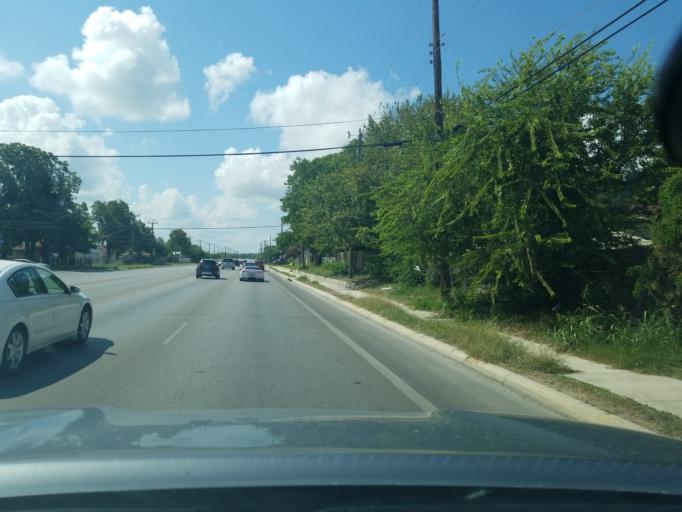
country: US
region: Texas
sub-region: Bexar County
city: San Antonio
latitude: 29.3439
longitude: -98.5343
